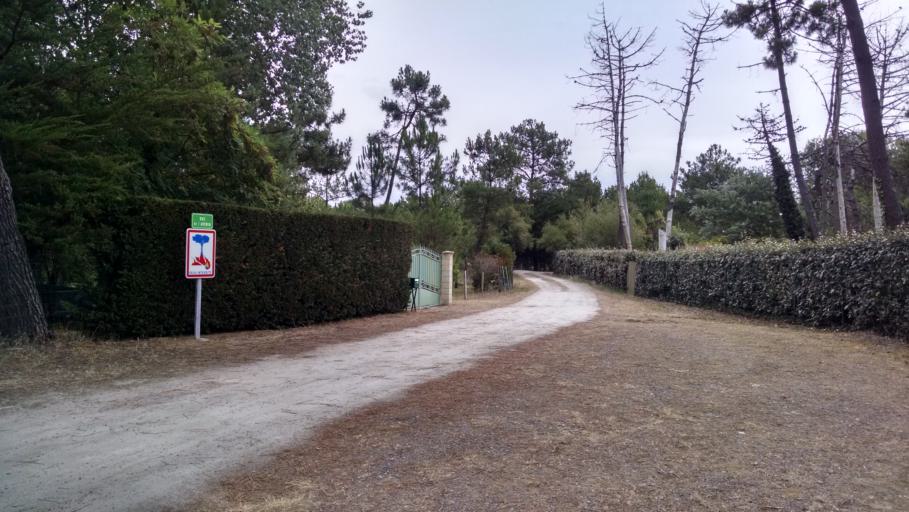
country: FR
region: Poitou-Charentes
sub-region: Departement de la Charente-Maritime
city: Saint-Martin-de-Re
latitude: 46.3093
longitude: -1.3042
